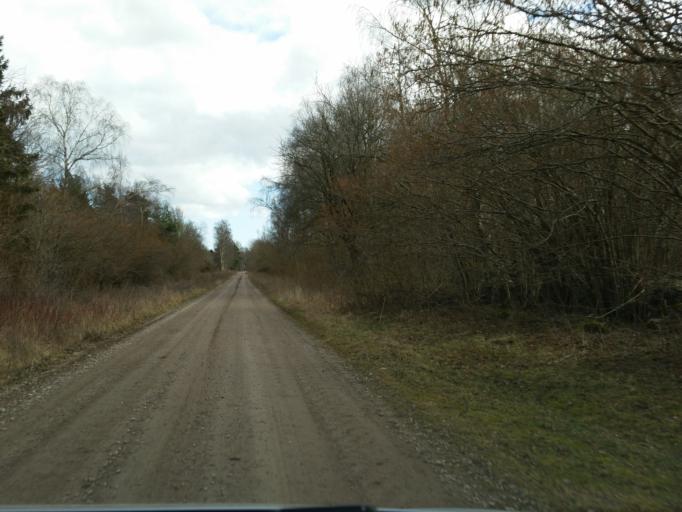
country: SE
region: Kalmar
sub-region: Morbylanga Kommun
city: Sodra Sandby
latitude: 56.6765
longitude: 16.6209
